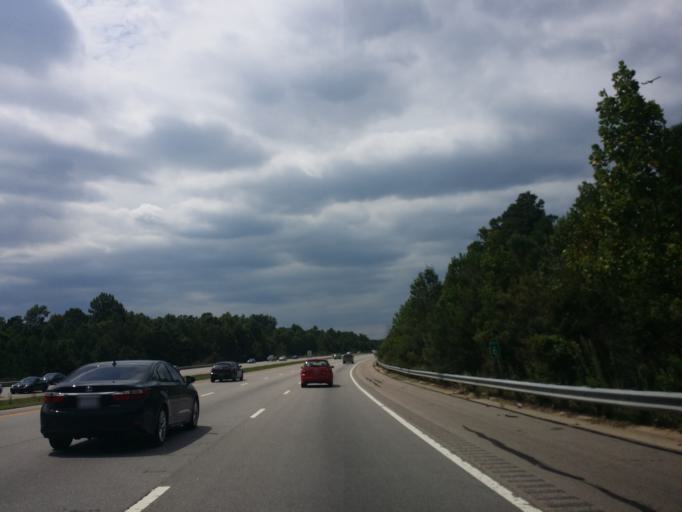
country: US
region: North Carolina
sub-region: Wake County
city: Morrisville
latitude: 35.9092
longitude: -78.7421
